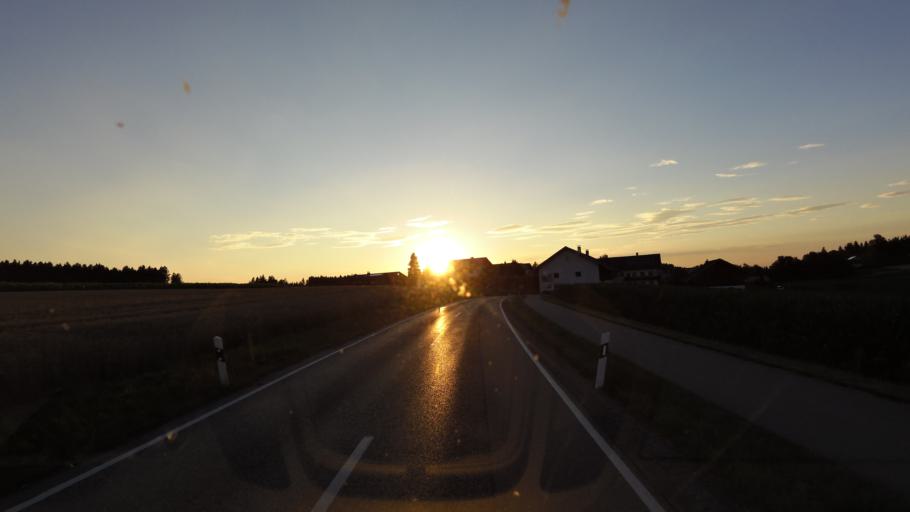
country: DE
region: Bavaria
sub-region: Upper Bavaria
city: Trostberg an der Alz
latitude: 48.0363
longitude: 12.5259
